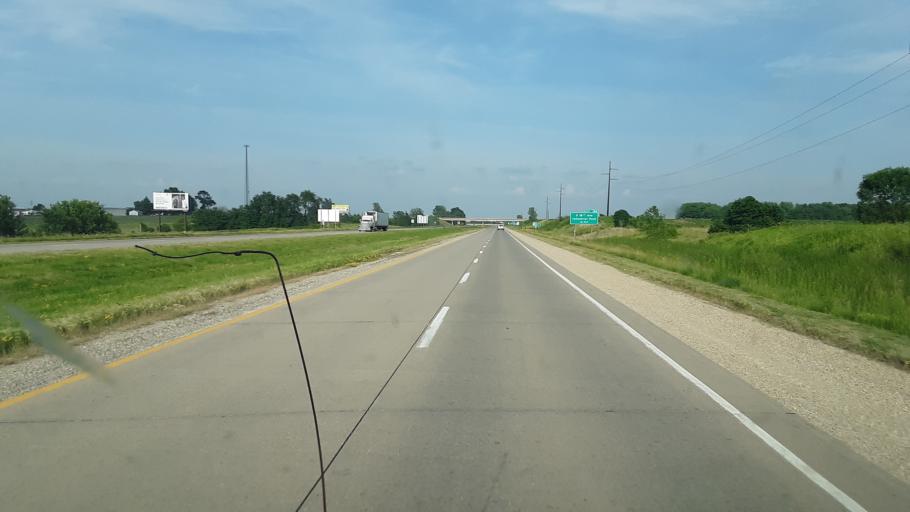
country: US
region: Iowa
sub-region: Marshall County
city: Marshalltown
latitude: 42.0034
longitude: -92.9016
